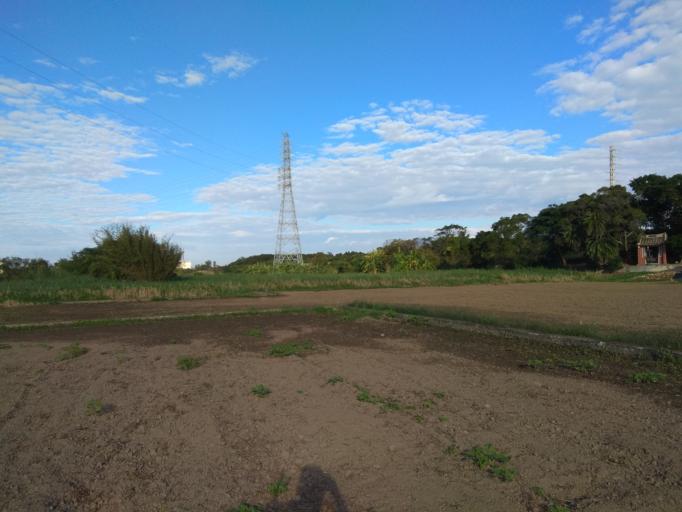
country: TW
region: Taiwan
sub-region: Hsinchu
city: Zhubei
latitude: 24.9858
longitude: 121.0383
